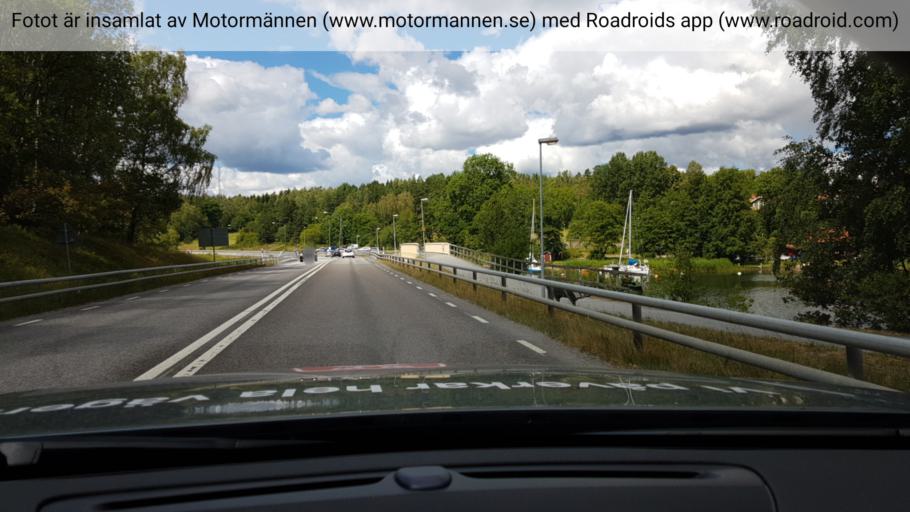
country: SE
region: Stockholm
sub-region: Vaxholms Kommun
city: Resaro
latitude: 59.4158
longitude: 18.3122
